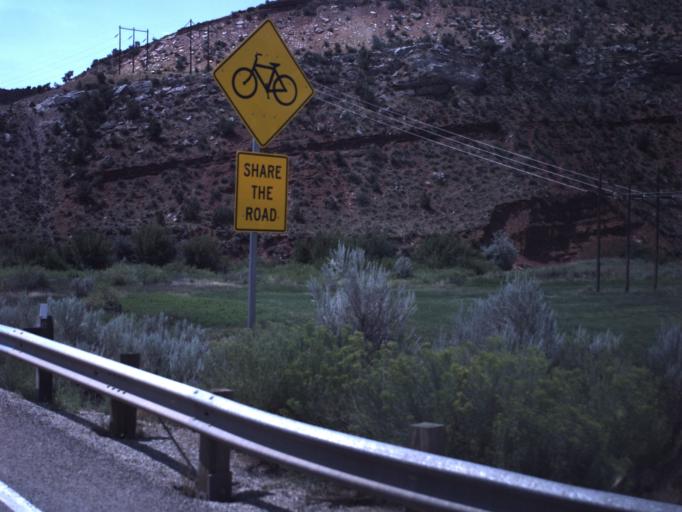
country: US
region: Utah
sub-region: Uintah County
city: Vernal
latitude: 40.5909
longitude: -109.4681
